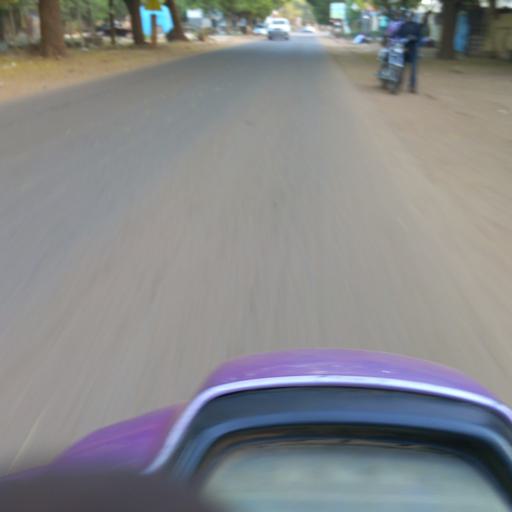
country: ML
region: Bamako
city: Bamako
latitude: 12.6522
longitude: -8.0134
